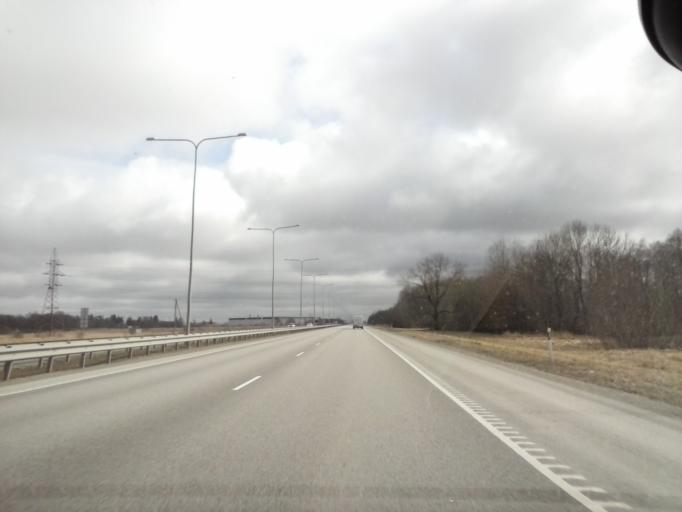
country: EE
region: Harju
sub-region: Rae vald
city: Jueri
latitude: 59.3727
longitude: 24.8521
